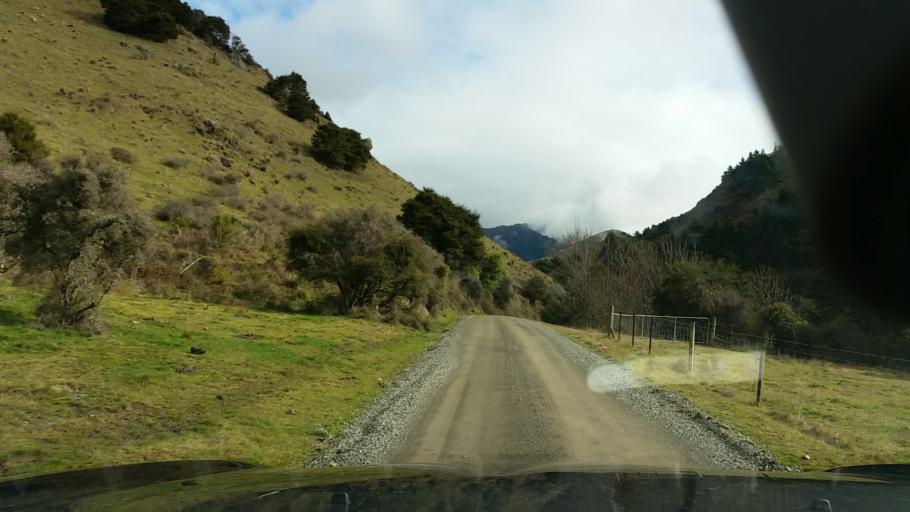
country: NZ
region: Tasman
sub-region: Tasman District
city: Richmond
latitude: -41.7311
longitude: 173.4639
